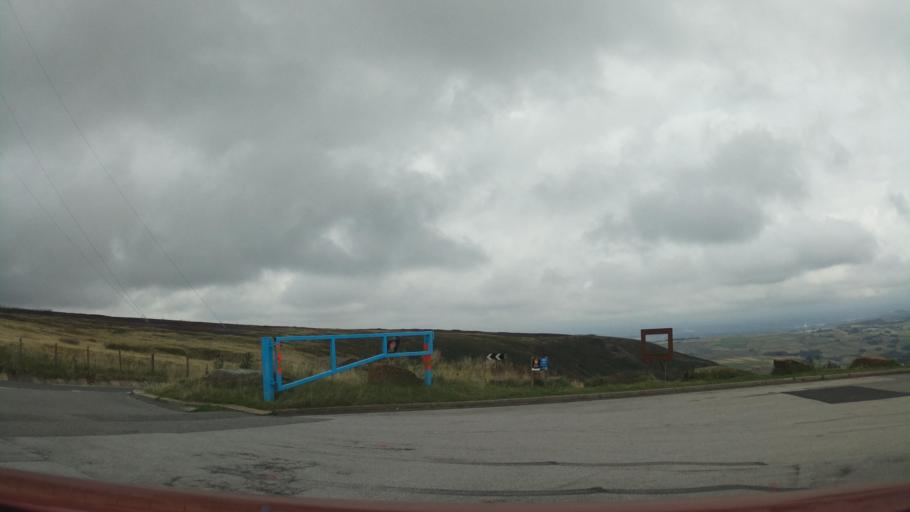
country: GB
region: England
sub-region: Kirklees
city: Meltham
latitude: 53.5318
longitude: -1.8540
